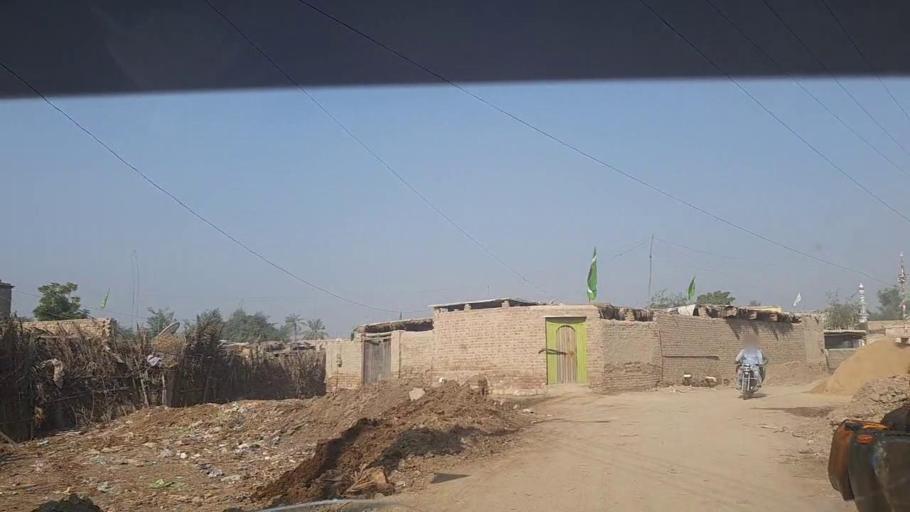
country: PK
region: Sindh
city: Khairpur
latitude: 27.4689
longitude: 68.7131
